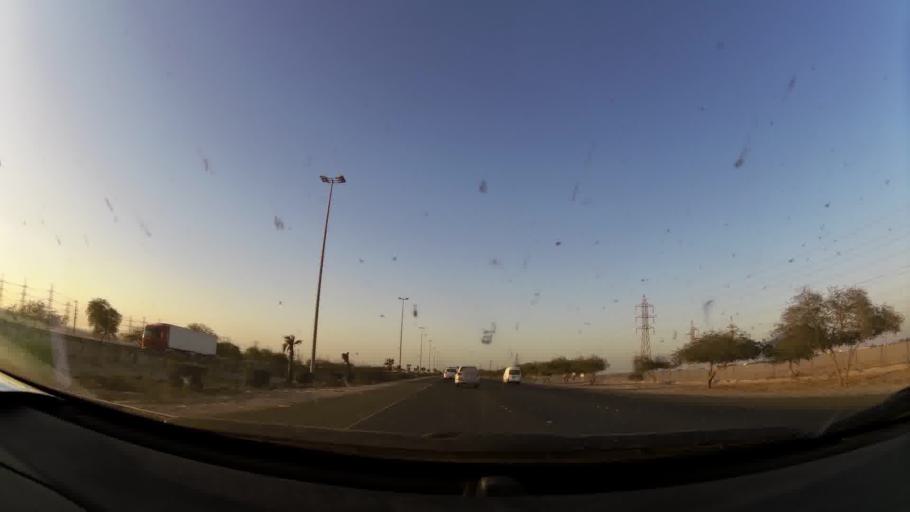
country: KW
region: Al Ahmadi
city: Al Fahahil
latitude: 28.8749
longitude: 48.2322
